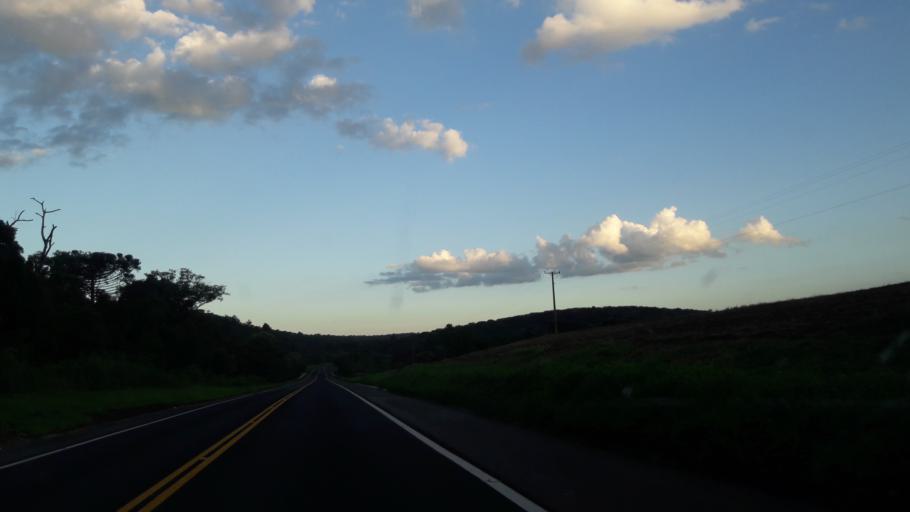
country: BR
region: Parana
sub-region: Irati
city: Irati
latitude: -25.4527
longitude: -50.4491
